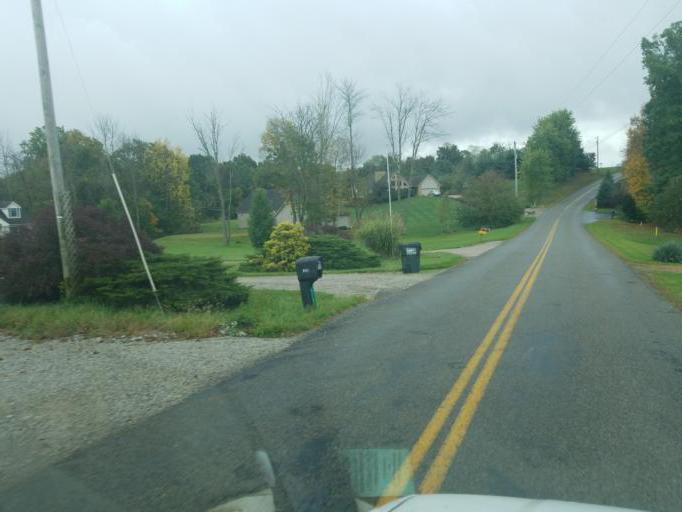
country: US
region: Ohio
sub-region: Holmes County
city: Millersburg
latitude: 40.5574
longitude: -82.0047
